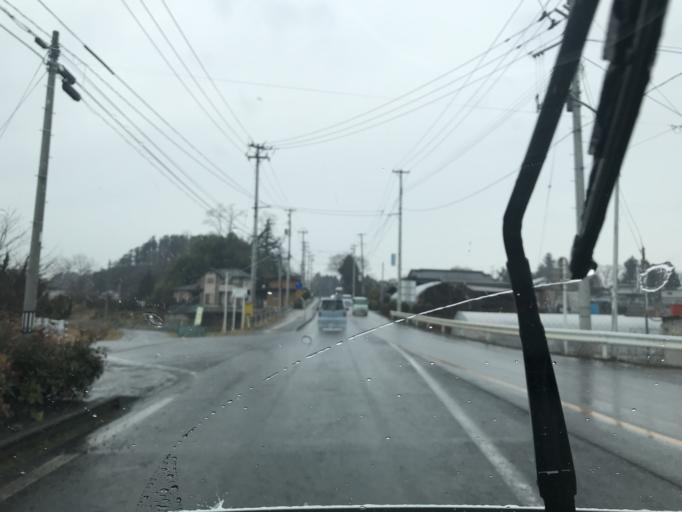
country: JP
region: Miyagi
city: Wakuya
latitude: 38.6909
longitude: 141.1800
